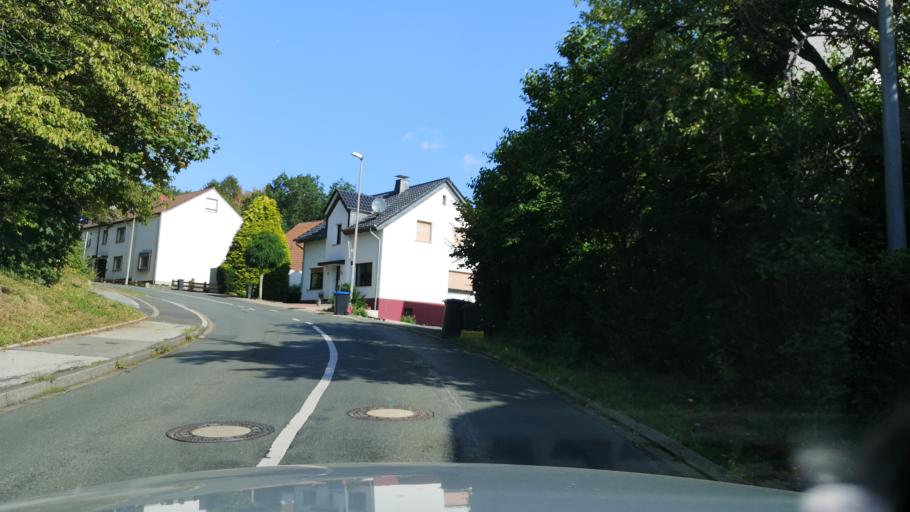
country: DE
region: North Rhine-Westphalia
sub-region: Regierungsbezirk Arnsberg
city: Frondenberg
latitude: 51.4852
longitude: 7.7667
